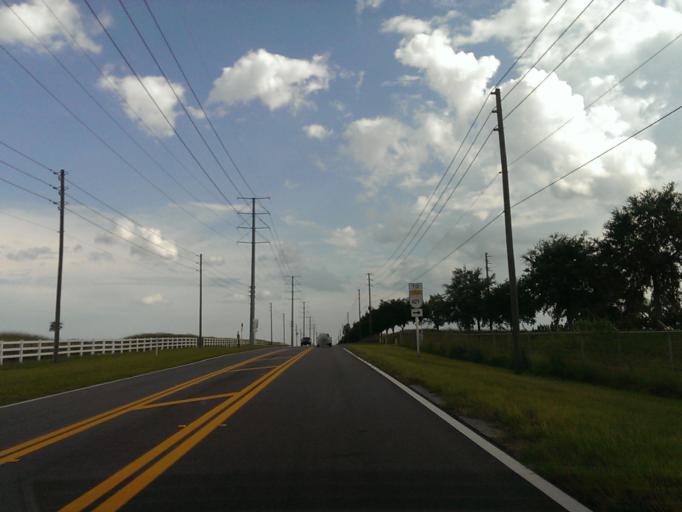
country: US
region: Florida
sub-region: Orange County
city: Oakland
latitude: 28.4500
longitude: -81.6362
